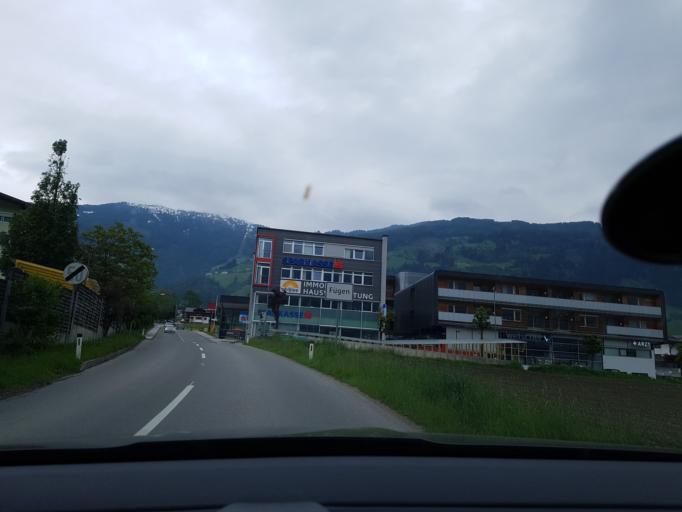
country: AT
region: Tyrol
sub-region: Politischer Bezirk Schwaz
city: Fugen
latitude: 47.3400
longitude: 11.8516
